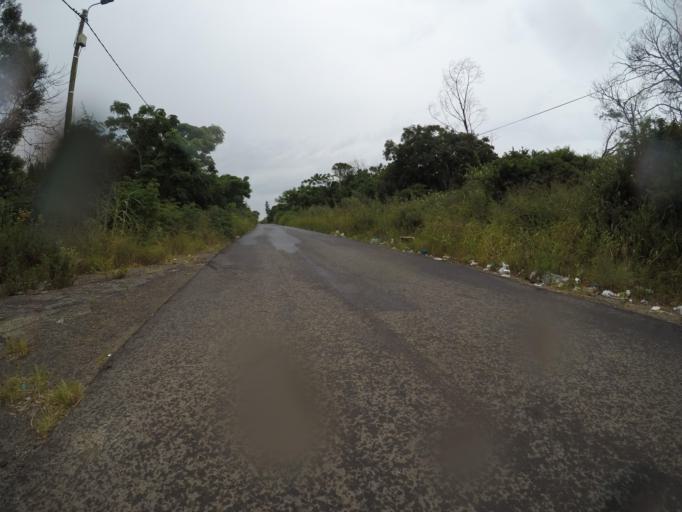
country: ZA
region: Eastern Cape
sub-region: Buffalo City Metropolitan Municipality
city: East London
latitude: -32.9700
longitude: 27.8276
